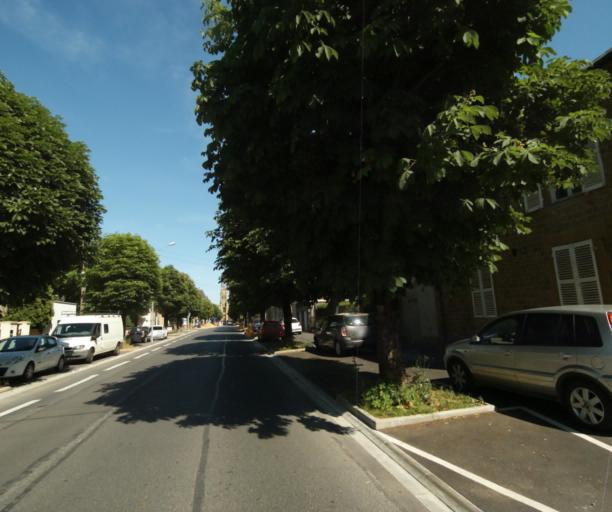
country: FR
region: Champagne-Ardenne
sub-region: Departement des Ardennes
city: Charleville-Mezieres
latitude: 49.7616
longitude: 4.7091
